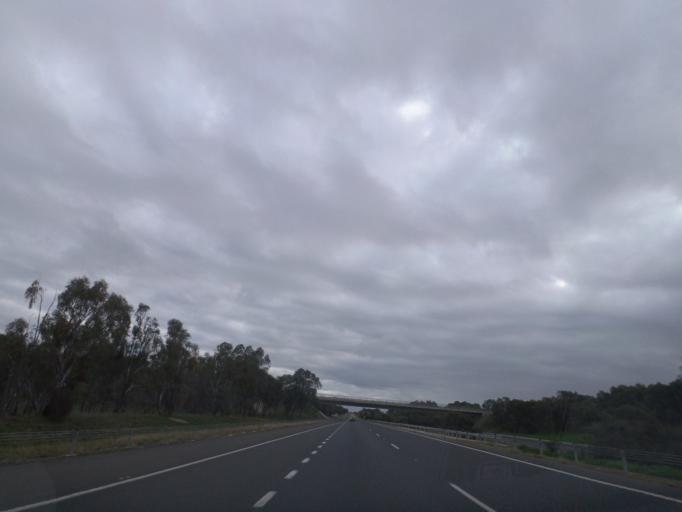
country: AU
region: New South Wales
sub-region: Corowa Shire
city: Howlong
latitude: -36.0826
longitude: 146.7301
